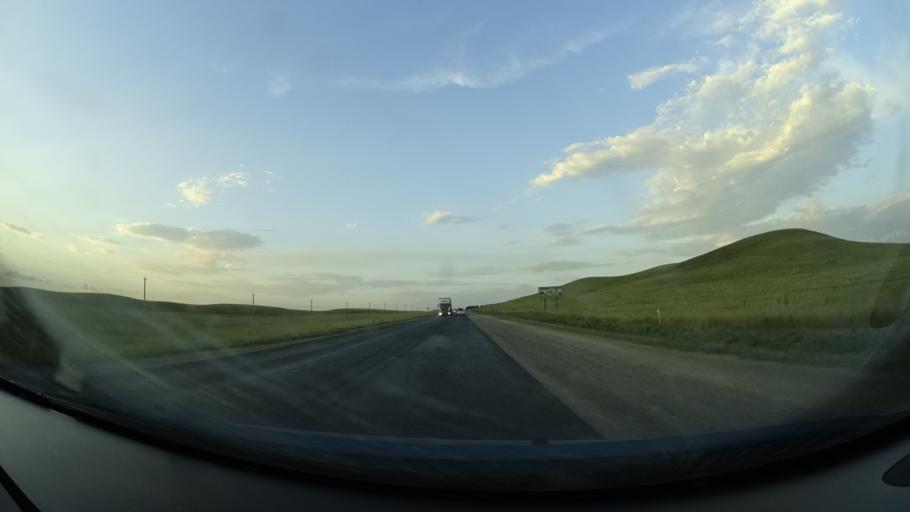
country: RU
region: Orenburg
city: Severnoye
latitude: 54.1389
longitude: 52.6006
